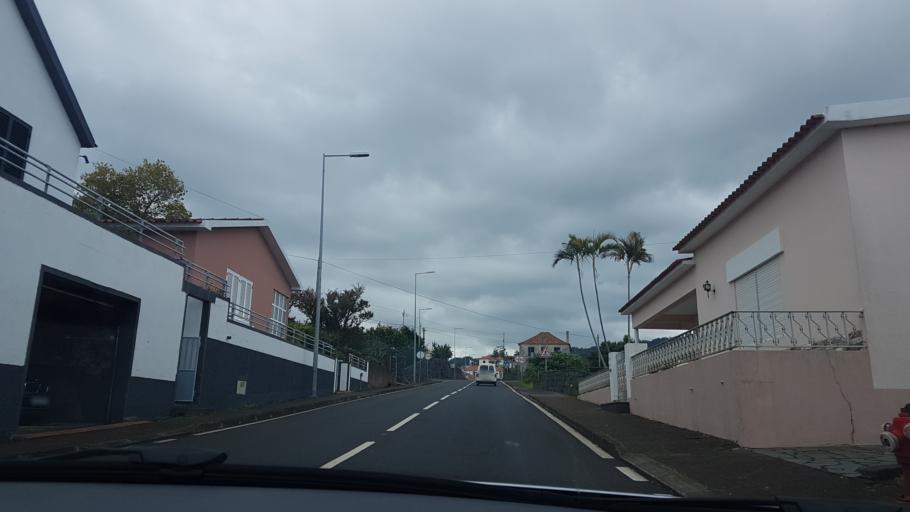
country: PT
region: Madeira
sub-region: Santana
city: Santana
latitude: 32.8191
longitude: -16.8876
